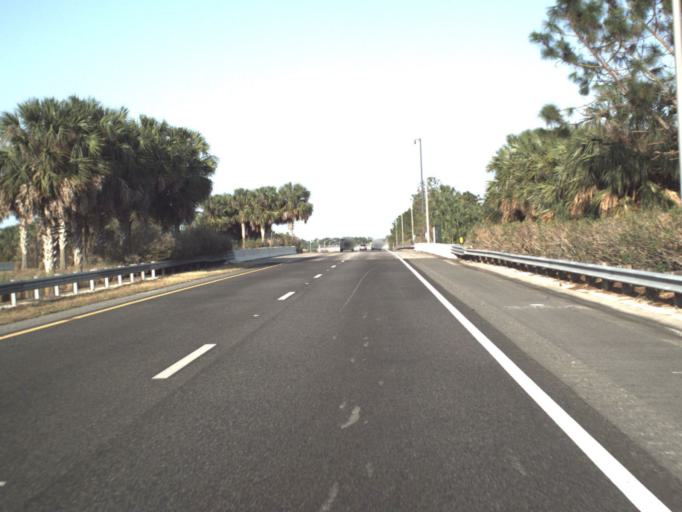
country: US
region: Florida
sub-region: Orange County
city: Alafaya
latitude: 28.5497
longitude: -81.2047
